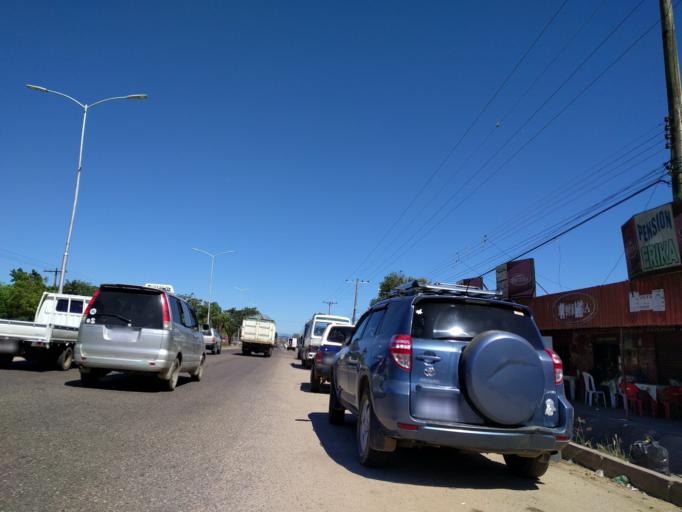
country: BO
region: Santa Cruz
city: Santa Cruz de la Sierra
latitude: -17.8621
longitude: -63.2652
